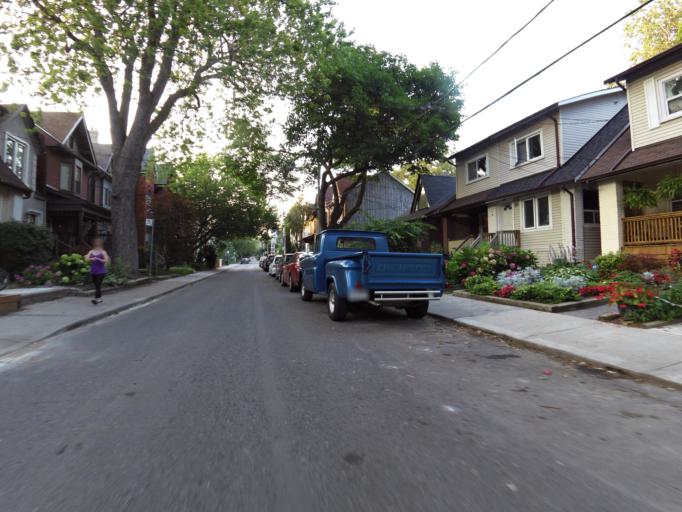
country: CA
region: Ontario
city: Toronto
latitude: 43.6620
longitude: -79.3468
